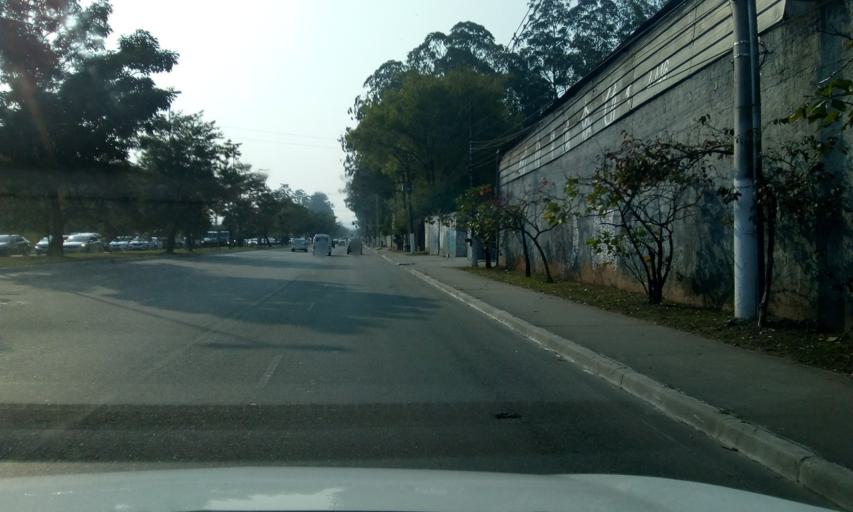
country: BR
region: Sao Paulo
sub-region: Diadema
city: Diadema
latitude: -23.6934
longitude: -46.6839
